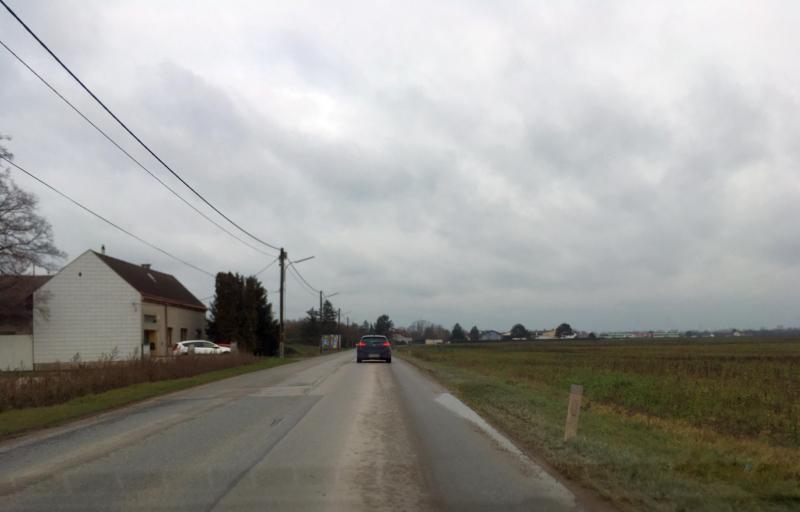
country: AT
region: Lower Austria
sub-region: Politischer Bezirk Ganserndorf
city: Aderklaa
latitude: 48.2444
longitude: 16.4937
